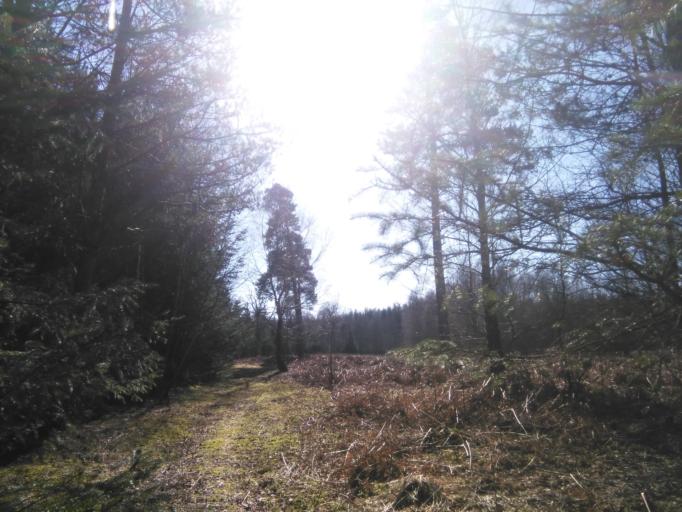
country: DK
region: Central Jutland
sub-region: Skanderborg Kommune
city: Ry
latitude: 56.1083
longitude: 9.7185
